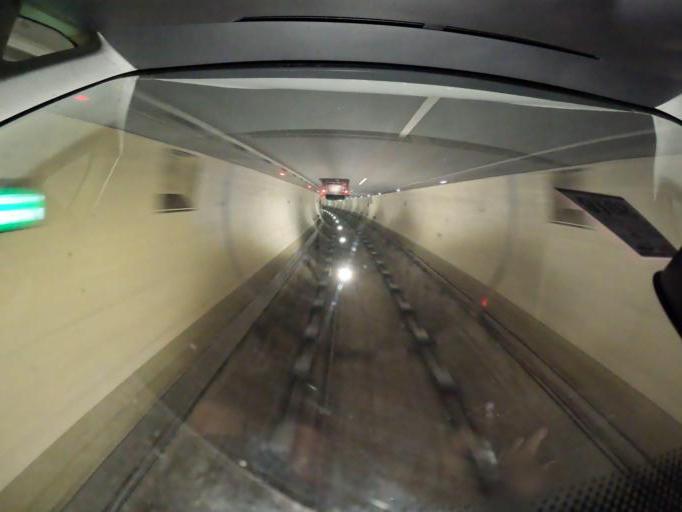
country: AT
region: Carinthia
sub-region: Politischer Bezirk Wolfsberg
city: Wolfsberg
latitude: 46.8990
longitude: 14.8205
